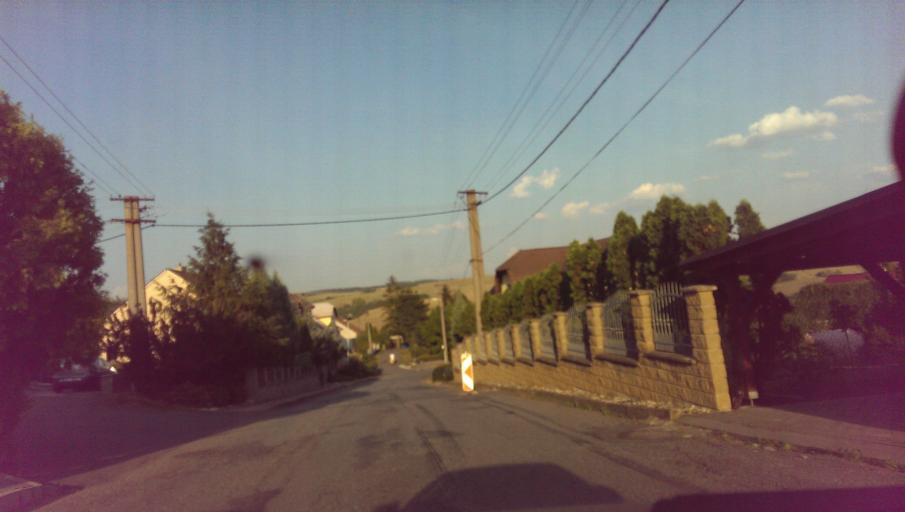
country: CZ
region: Zlin
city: Slusovice
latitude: 49.2379
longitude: 17.7833
